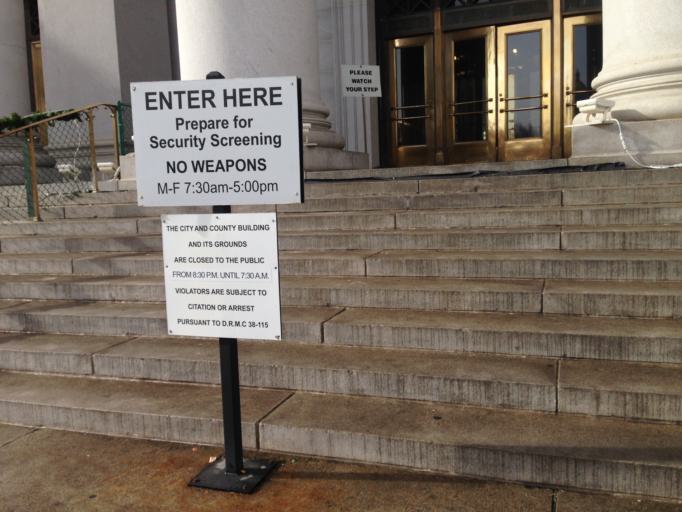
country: US
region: Colorado
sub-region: Denver County
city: Denver
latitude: 39.7393
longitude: -104.9908
